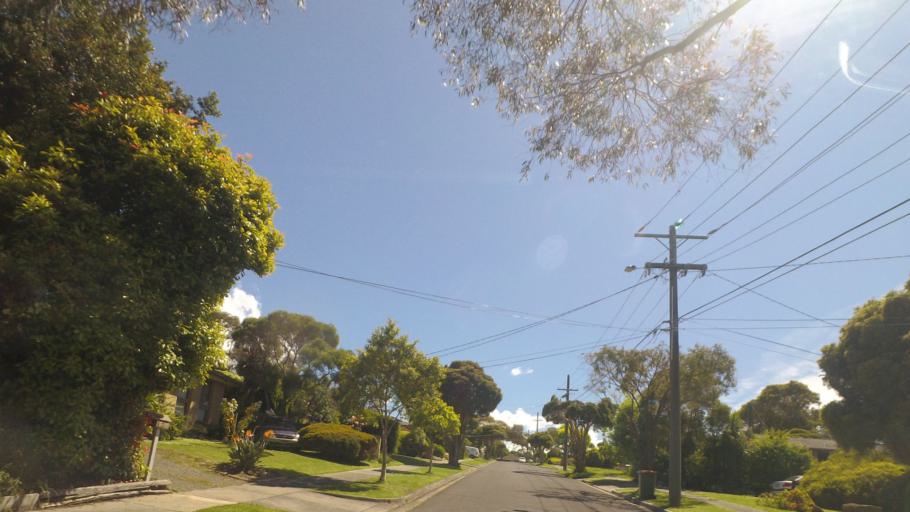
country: AU
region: Victoria
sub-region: Maroondah
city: Croydon South
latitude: -37.8187
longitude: 145.2773
